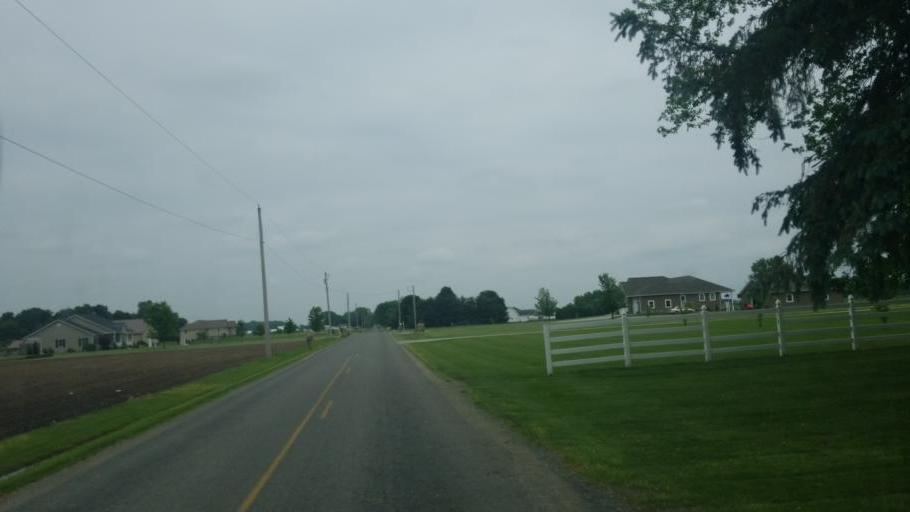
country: US
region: Indiana
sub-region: Elkhart County
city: Nappanee
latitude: 41.4572
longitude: -86.0491
